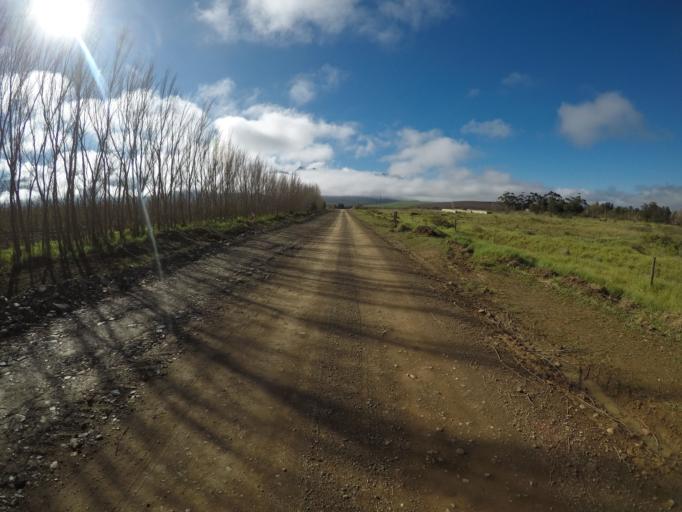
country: ZA
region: Western Cape
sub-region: Overberg District Municipality
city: Caledon
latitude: -34.1150
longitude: 19.7416
